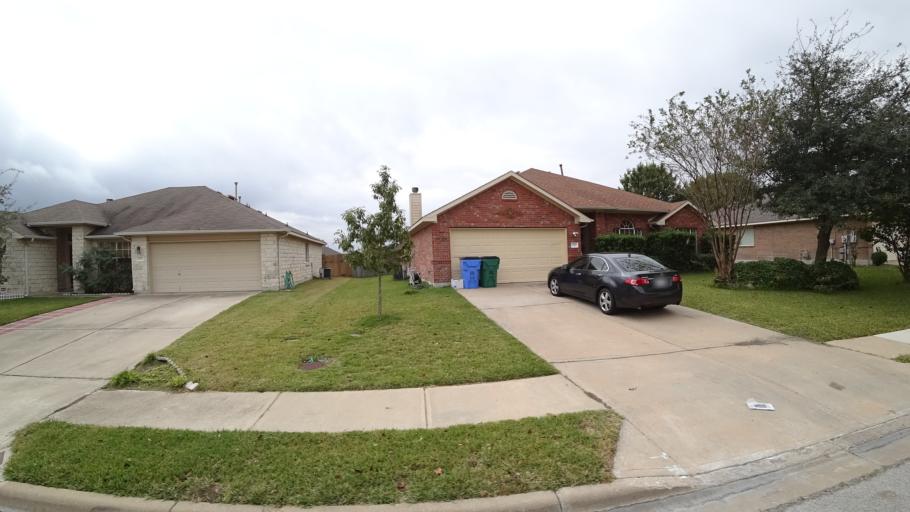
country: US
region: Texas
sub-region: Travis County
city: Pflugerville
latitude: 30.4365
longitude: -97.6041
